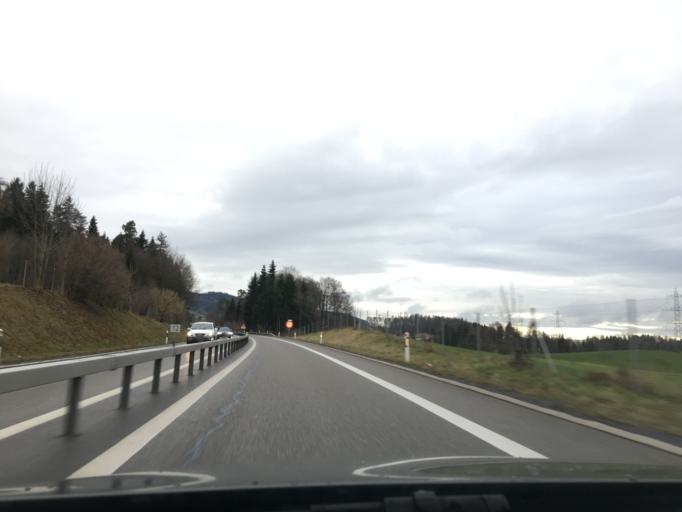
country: CH
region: Zurich
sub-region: Bezirk Uster
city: Esslingen
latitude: 47.2975
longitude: 8.7076
